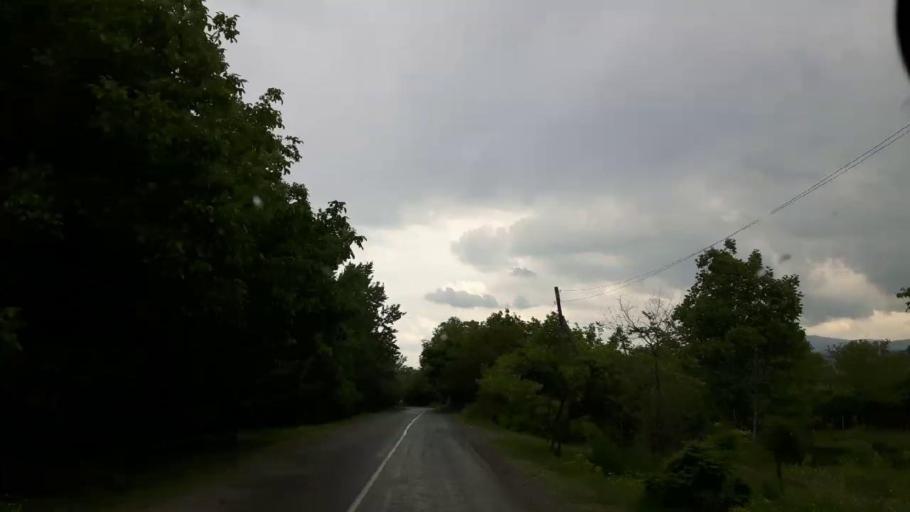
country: GE
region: Shida Kartli
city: Gori
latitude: 41.9614
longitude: 44.2175
